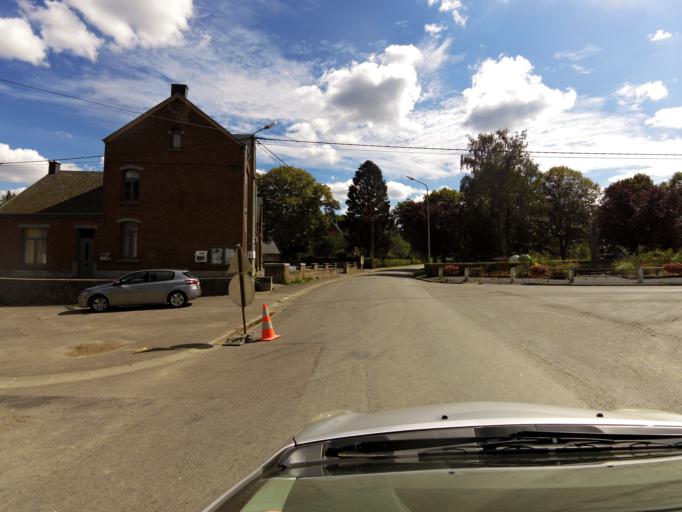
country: BE
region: Wallonia
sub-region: Province de Namur
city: Somme-Leuze
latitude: 50.3295
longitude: 5.4112
